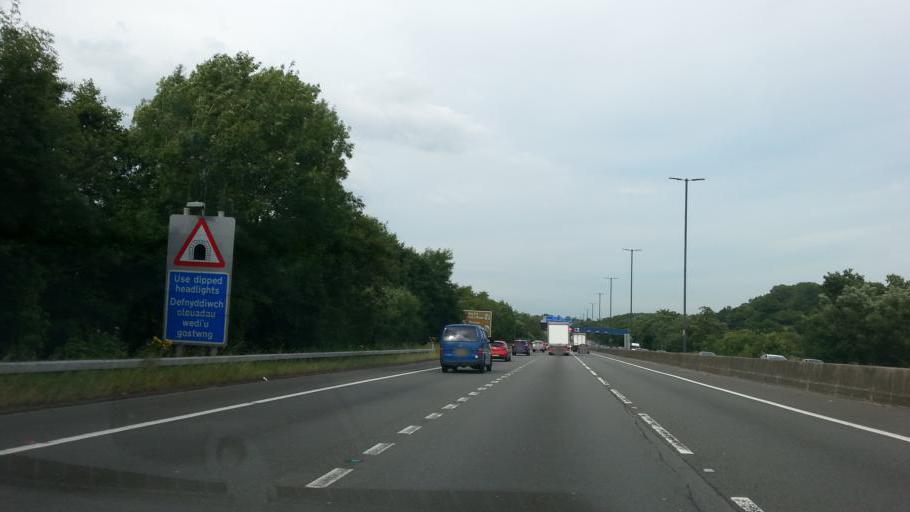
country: GB
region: Wales
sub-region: Newport
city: Newport
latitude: 51.5964
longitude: -3.0169
